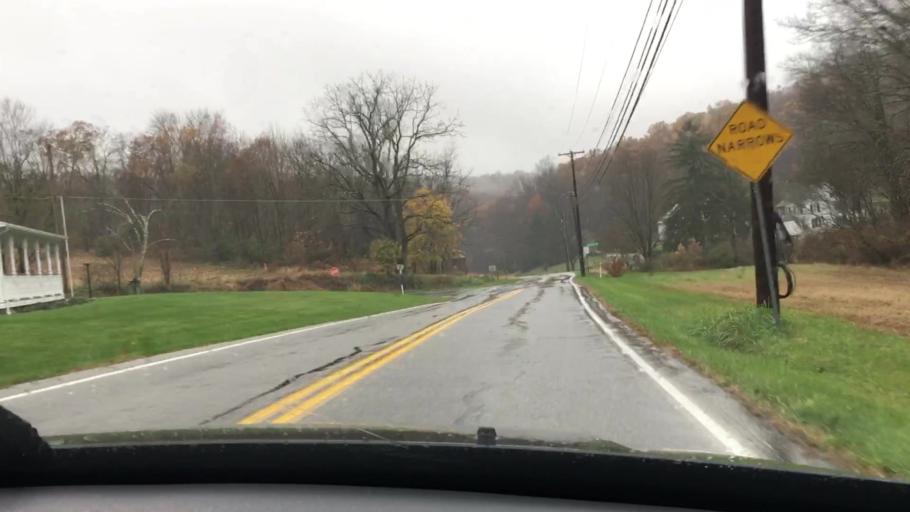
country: US
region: Pennsylvania
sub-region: York County
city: Glen Rock
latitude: 39.7667
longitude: -76.7417
